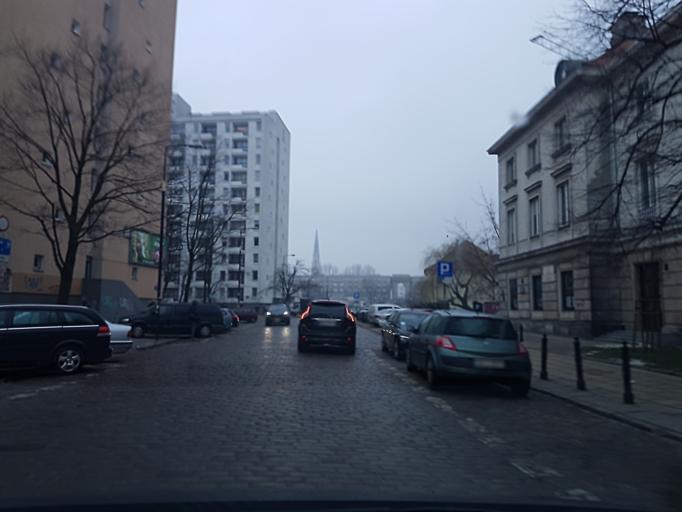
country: PL
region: Masovian Voivodeship
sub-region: Warszawa
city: Wola
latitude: 52.2461
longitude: 21.0034
